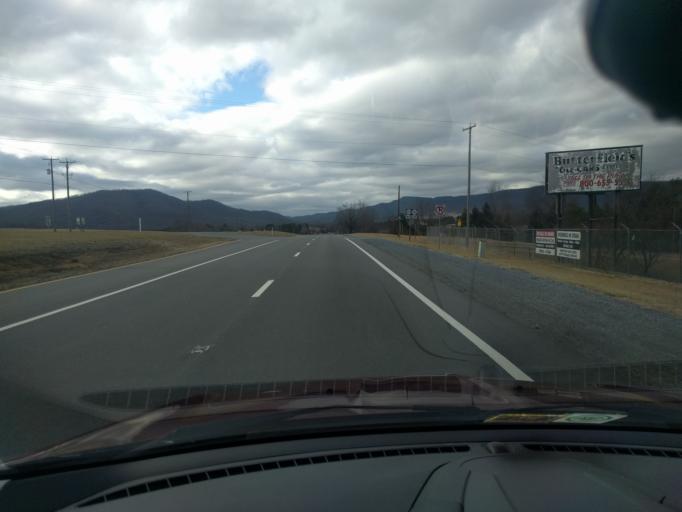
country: US
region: Virginia
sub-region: Botetourt County
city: Blue Ridge
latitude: 37.3771
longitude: -79.7092
